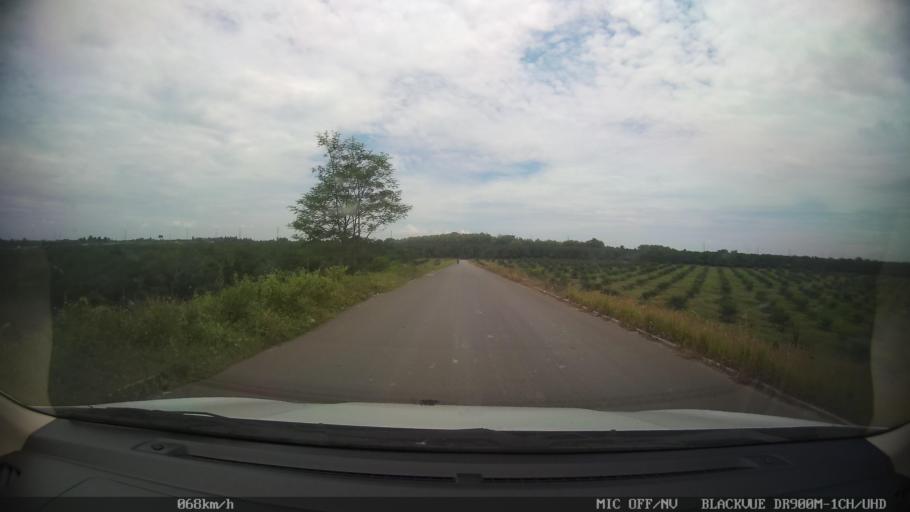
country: ID
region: North Sumatra
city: Sunggal
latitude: 3.6346
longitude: 98.5809
